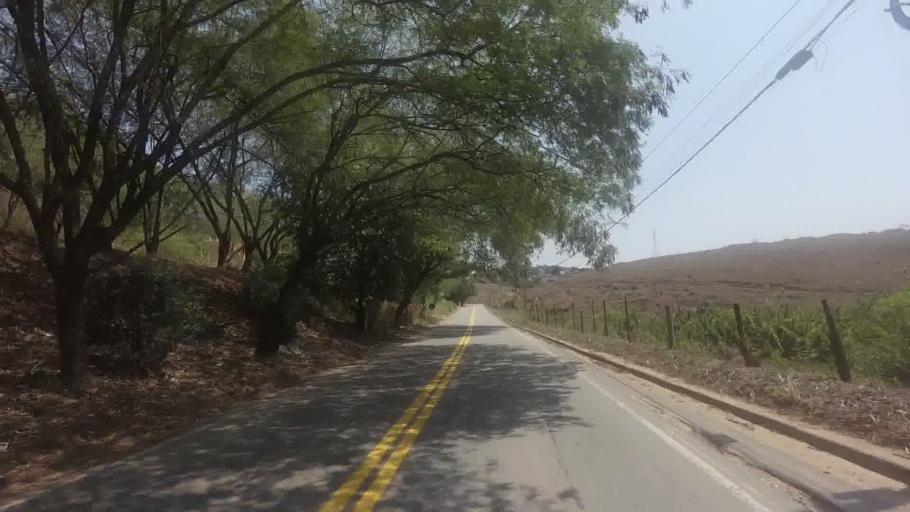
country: BR
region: Espirito Santo
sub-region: Cachoeiro De Itapemirim
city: Cachoeiro de Itapemirim
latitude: -20.8524
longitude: -41.0871
